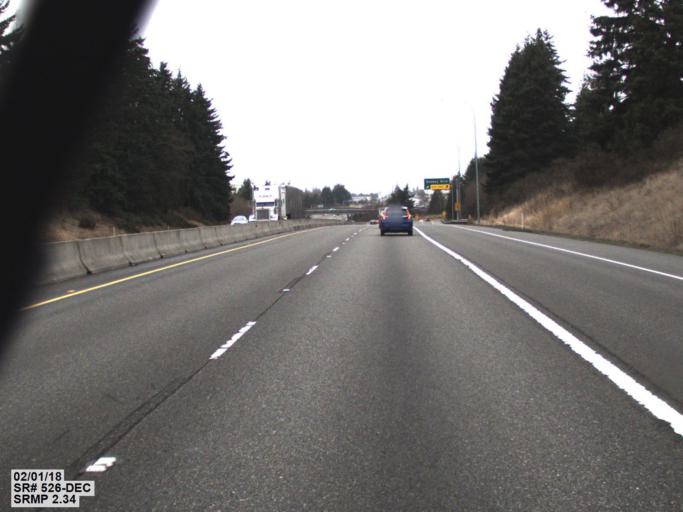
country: US
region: Washington
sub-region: Snohomish County
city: Mukilteo
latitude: 47.9233
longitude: -122.2526
